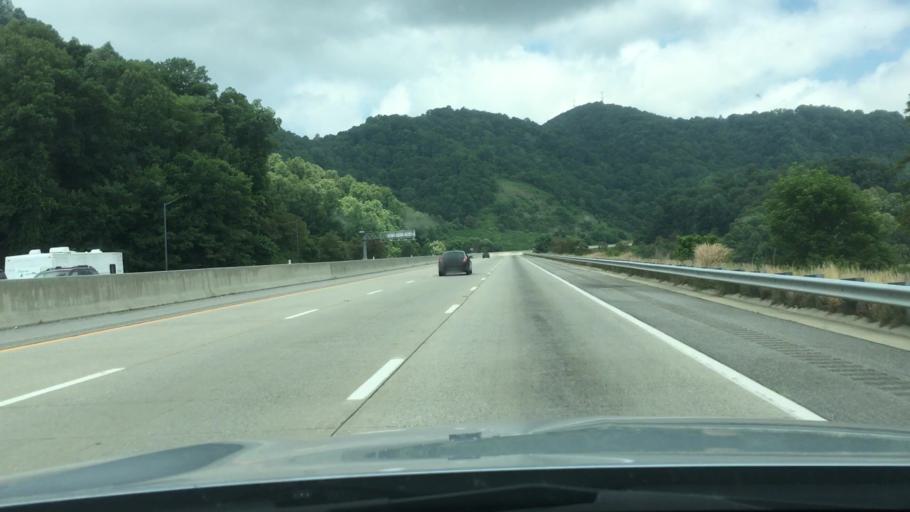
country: US
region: North Carolina
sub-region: Madison County
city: Mars Hill
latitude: 35.8758
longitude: -82.5443
